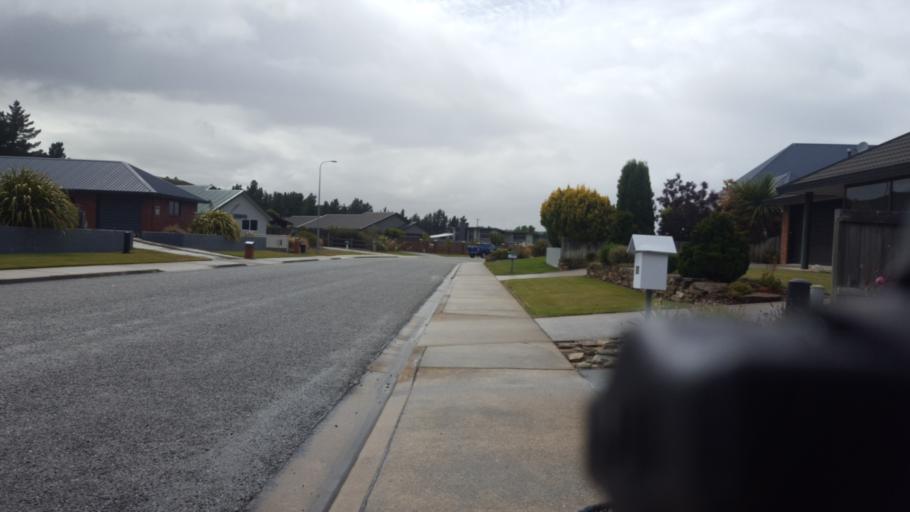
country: NZ
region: Otago
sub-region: Queenstown-Lakes District
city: Wanaka
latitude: -45.1940
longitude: 169.3324
